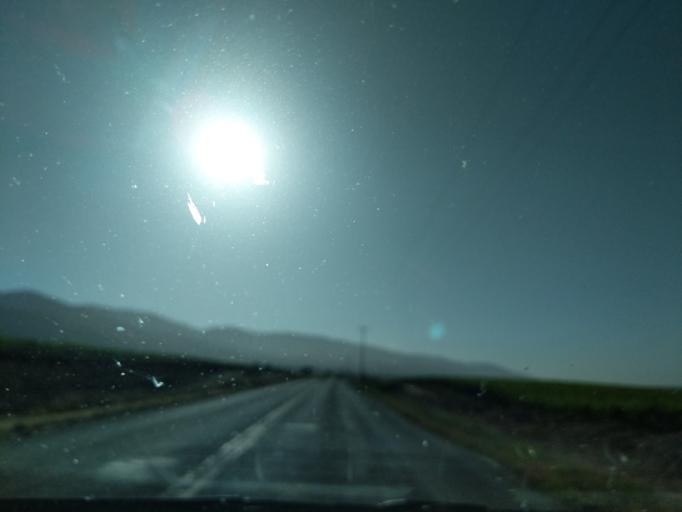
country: US
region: California
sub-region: Monterey County
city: Soledad
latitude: 36.4292
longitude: -121.4082
